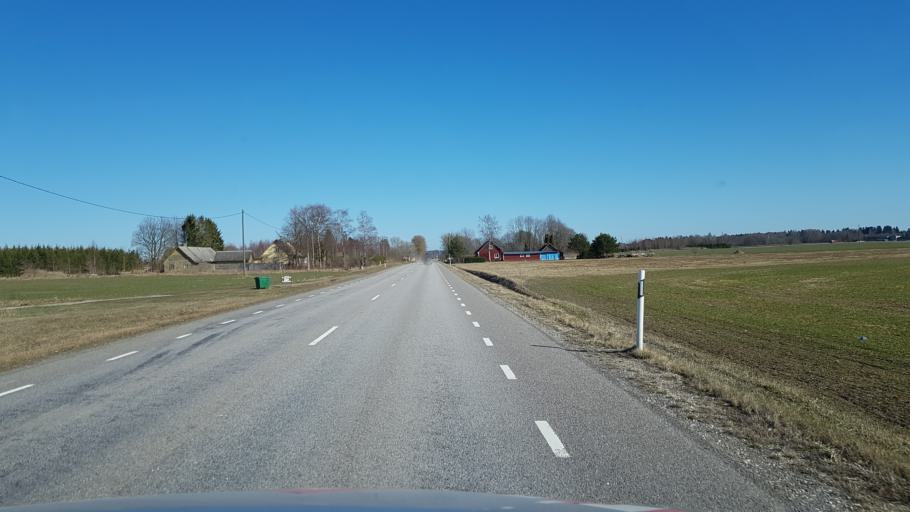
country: EE
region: Laeaene-Virumaa
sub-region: Viru-Nigula vald
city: Kunda
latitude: 59.3550
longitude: 26.6628
